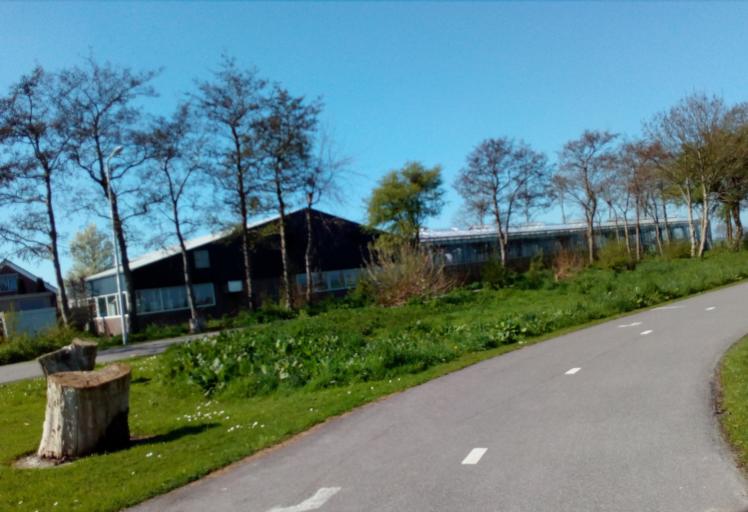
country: NL
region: South Holland
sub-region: Gemeente Westland
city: De Lier
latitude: 51.9811
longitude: 4.2993
